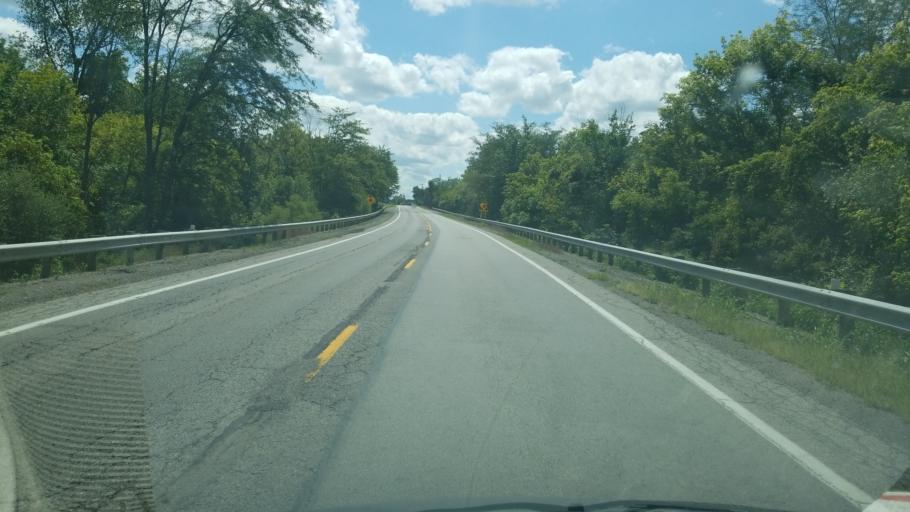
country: US
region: Ohio
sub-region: Henry County
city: Liberty Center
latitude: 41.4161
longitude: -84.0092
